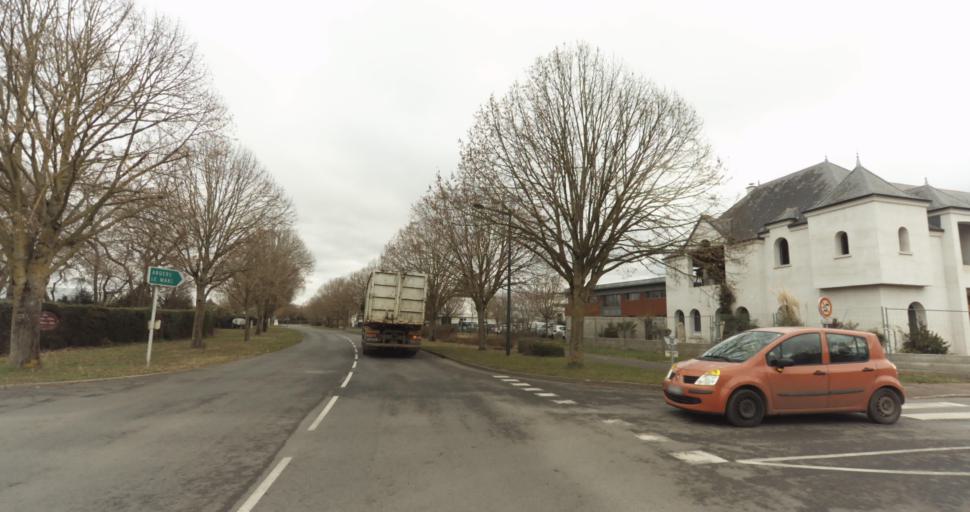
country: FR
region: Pays de la Loire
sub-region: Departement de Maine-et-Loire
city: Saumur
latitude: 47.2734
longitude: -0.0695
